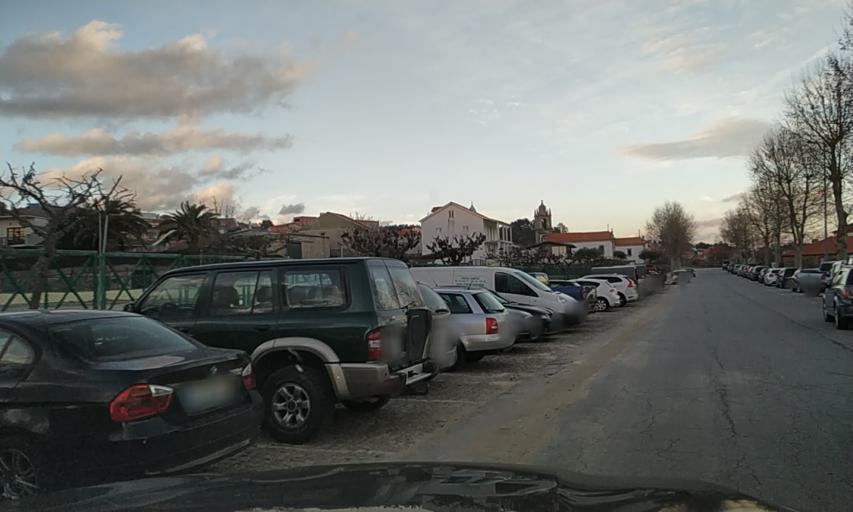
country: PT
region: Braganca
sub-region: Carrazeda de Ansiaes
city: Carrazeda de Anciaes
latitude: 41.2416
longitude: -7.3026
